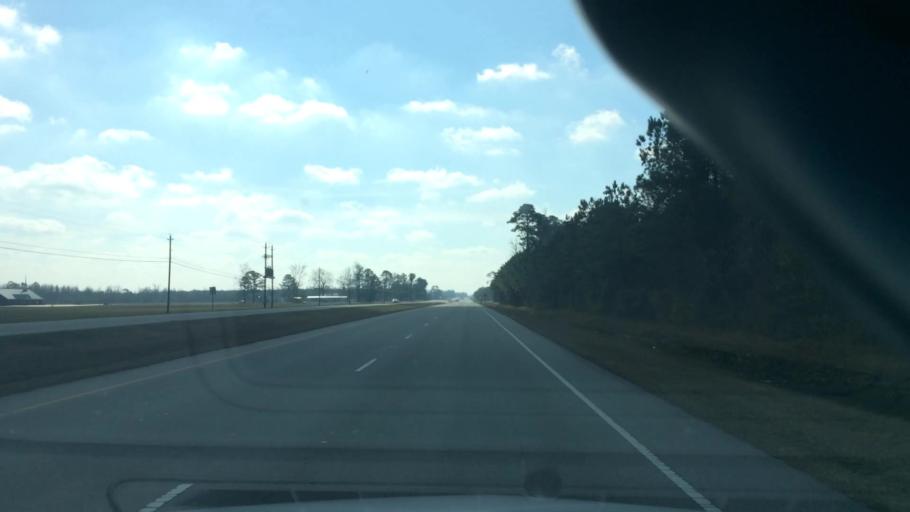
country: US
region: North Carolina
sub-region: Duplin County
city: Beulaville
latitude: 35.1146
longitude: -77.7173
